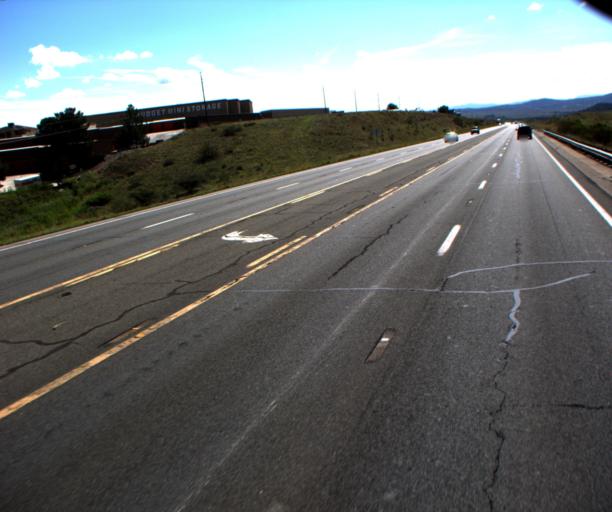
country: US
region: Arizona
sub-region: Yavapai County
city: Prescott Valley
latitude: 34.5827
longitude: -112.3077
